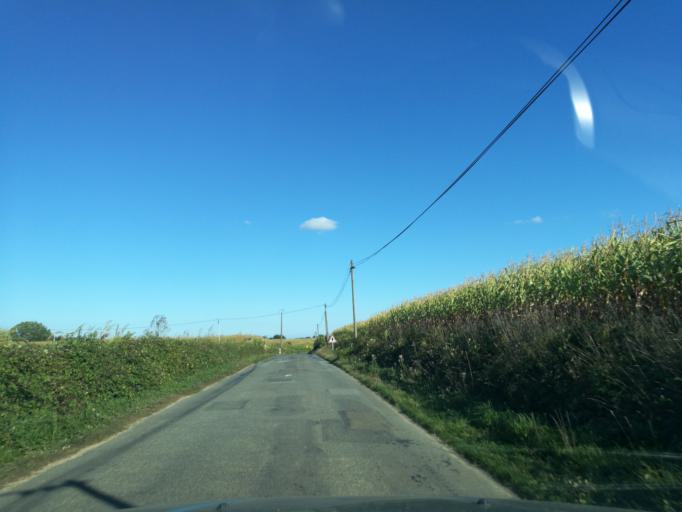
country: FR
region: Brittany
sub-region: Departement d'Ille-et-Vilaine
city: Montauban-de-Bretagne
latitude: 48.1725
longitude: -2.0203
